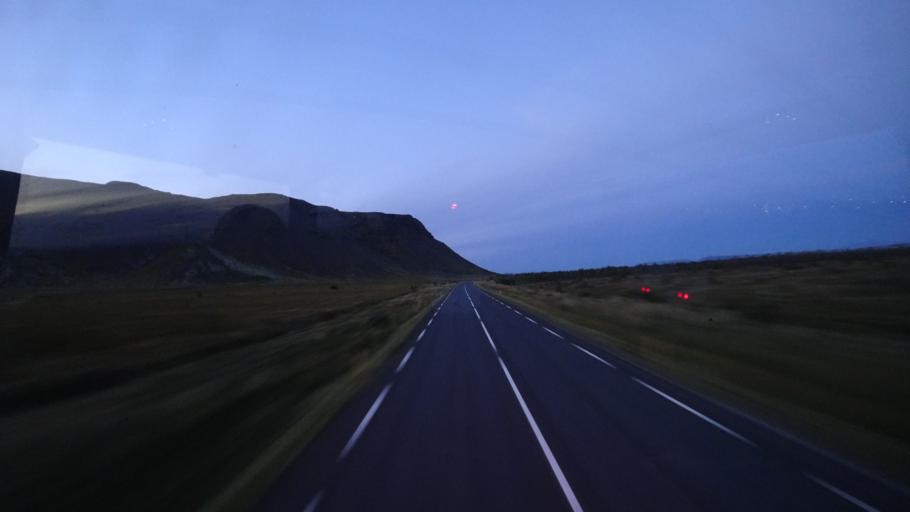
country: IS
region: South
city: Selfoss
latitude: 63.9538
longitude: -21.0177
